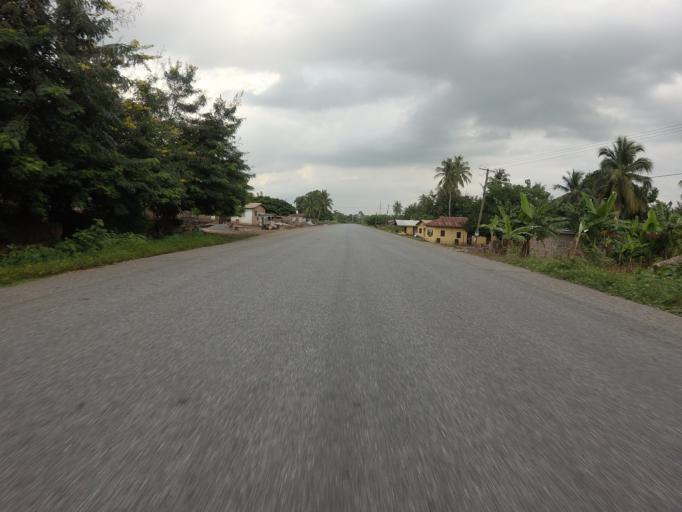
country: GH
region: Volta
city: Ho
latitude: 6.4839
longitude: 0.4926
